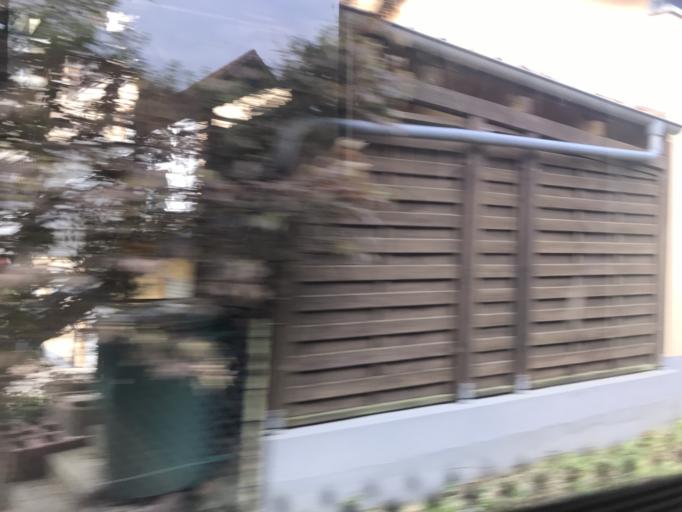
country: DE
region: Hesse
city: Kelkheim (Taunus)
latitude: 50.1240
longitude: 8.4631
